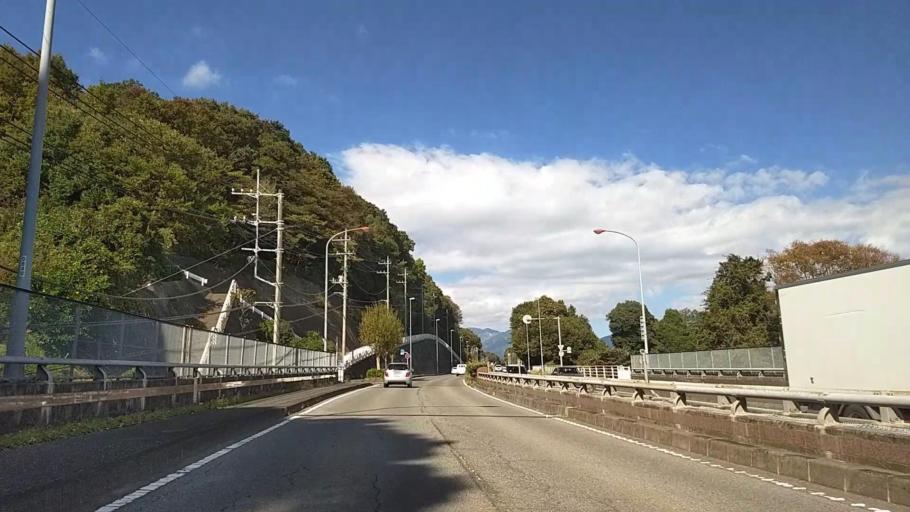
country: JP
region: Kanagawa
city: Ninomiya
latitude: 35.3285
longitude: 139.2329
